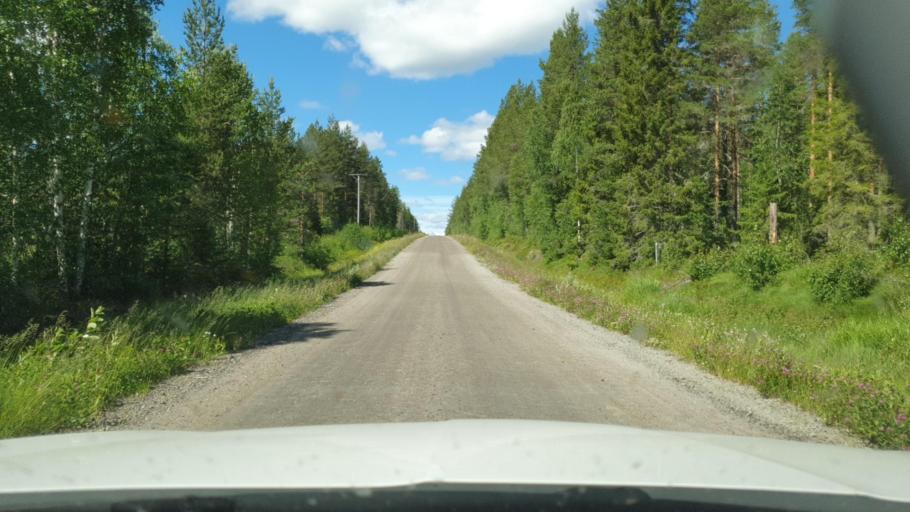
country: SE
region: Norrbotten
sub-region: Pitea Kommun
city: Roknas
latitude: 65.1603
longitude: 21.1534
